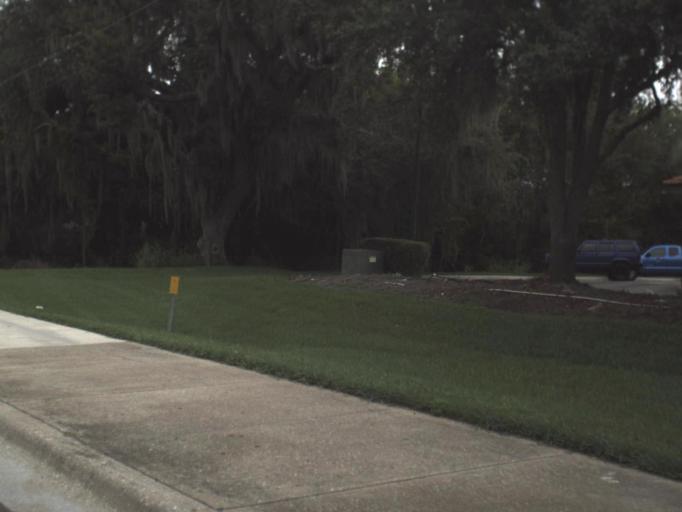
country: US
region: Florida
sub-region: Sarasota County
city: Lake Sarasota
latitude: 27.2990
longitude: -82.4552
